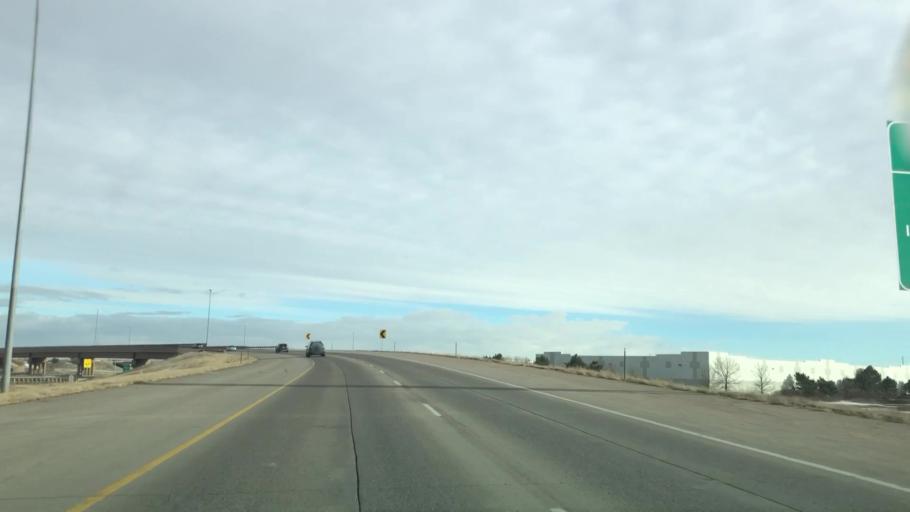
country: US
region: Colorado
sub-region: Adams County
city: Aurora
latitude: 39.7683
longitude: -104.7999
